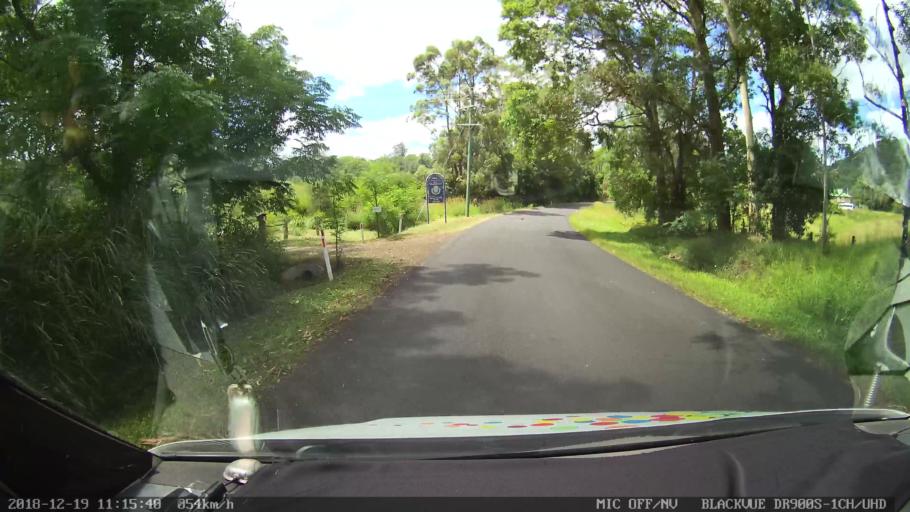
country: AU
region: New South Wales
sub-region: Lismore Municipality
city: Nimbin
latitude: -28.6698
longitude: 153.2786
